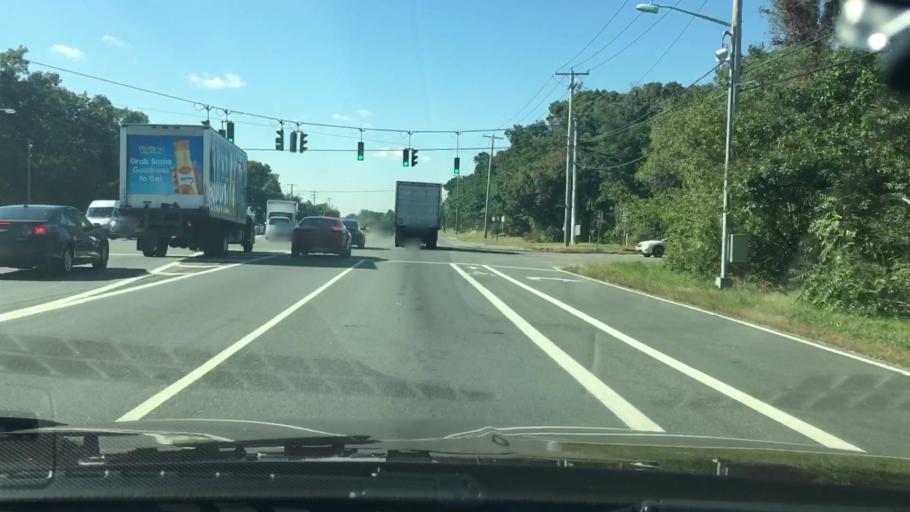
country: US
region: New York
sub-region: Suffolk County
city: Holbrook
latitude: 40.7820
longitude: -73.0837
